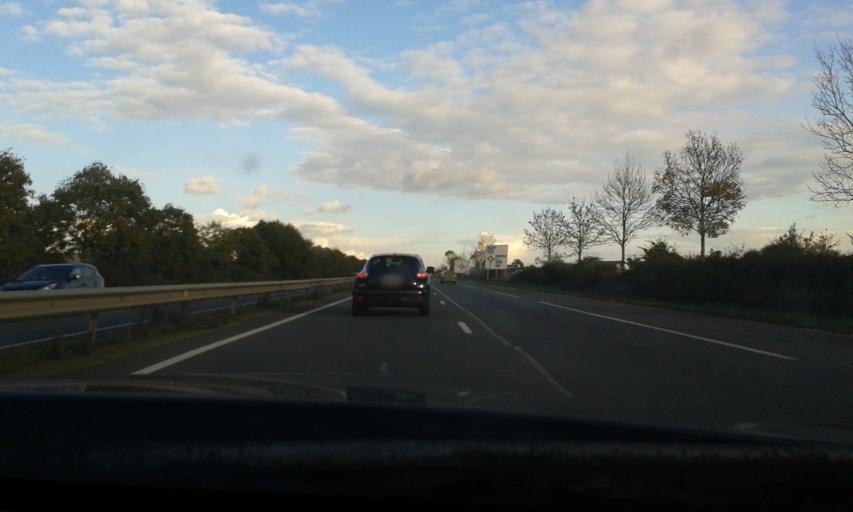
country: FR
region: Centre
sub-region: Departement d'Eure-et-Loir
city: Barjouville
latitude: 48.4160
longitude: 1.4548
